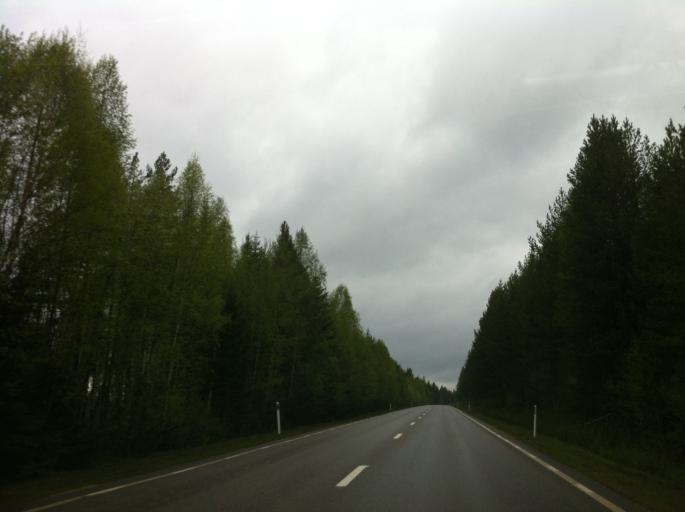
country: SE
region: Jaemtland
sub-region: Harjedalens Kommun
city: Sveg
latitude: 62.0998
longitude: 14.2191
